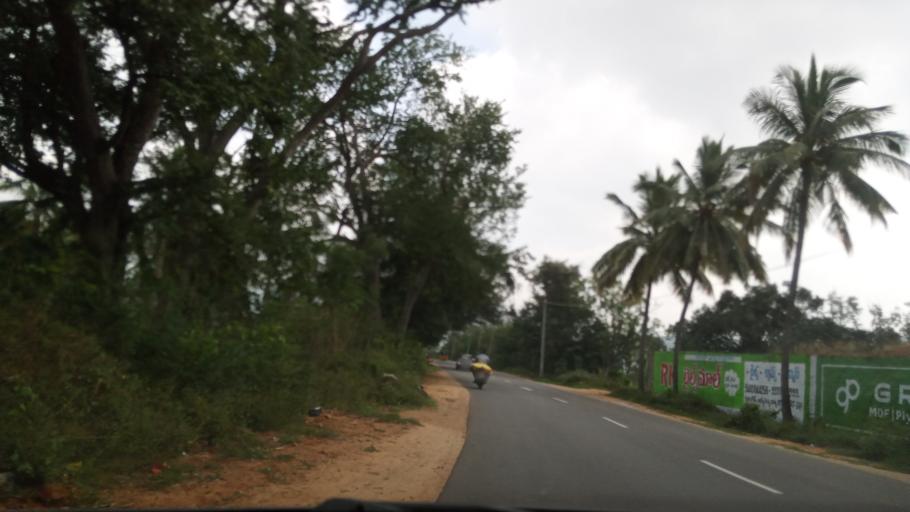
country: IN
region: Andhra Pradesh
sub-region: Chittoor
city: Madanapalle
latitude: 13.6401
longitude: 78.5737
